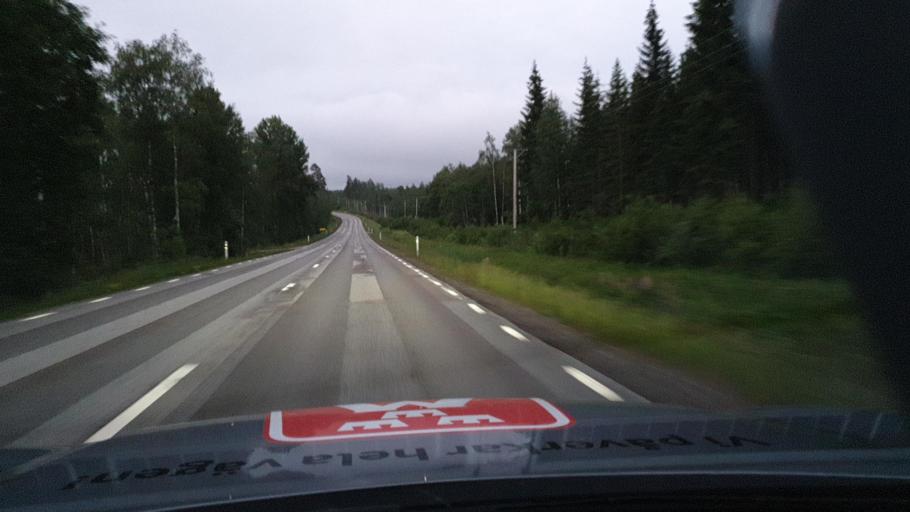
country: SE
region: OErebro
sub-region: Hallefors Kommun
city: Haellefors
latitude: 59.7697
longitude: 14.4016
